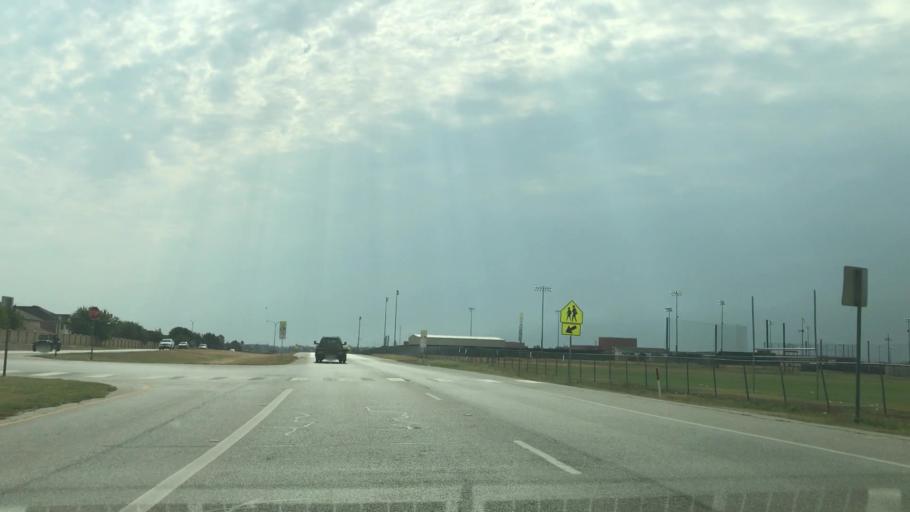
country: US
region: Texas
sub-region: Tarrant County
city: Blue Mound
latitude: 32.8951
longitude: -97.3012
